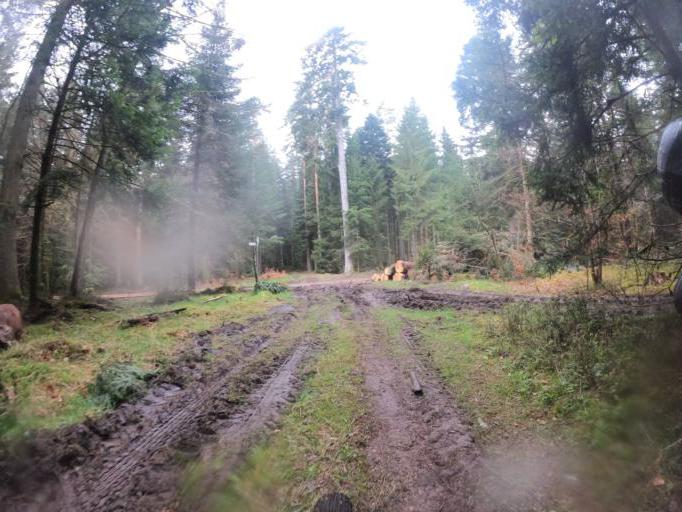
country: DE
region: Baden-Wuerttemberg
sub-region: Karlsruhe Region
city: Neuweiler
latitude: 48.6995
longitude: 8.6061
